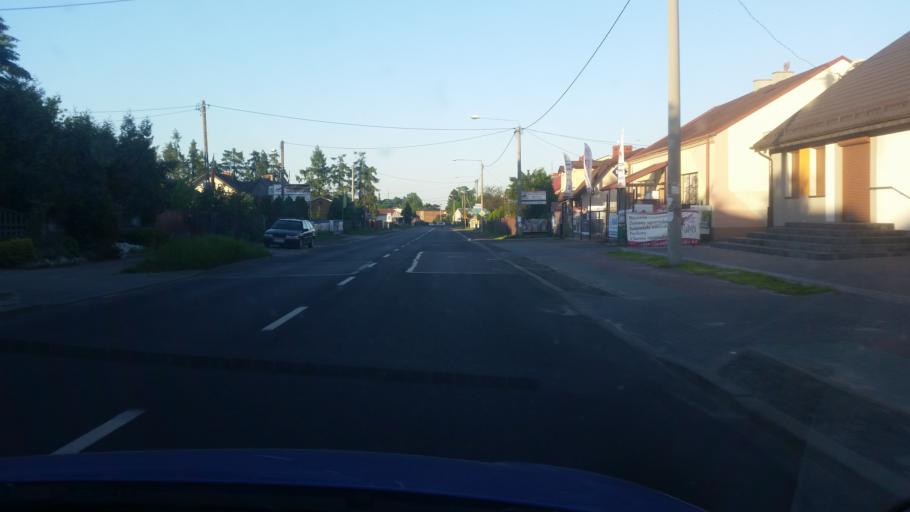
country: PL
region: Silesian Voivodeship
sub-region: Powiat czestochowski
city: Klomnice
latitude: 50.9201
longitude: 19.3511
